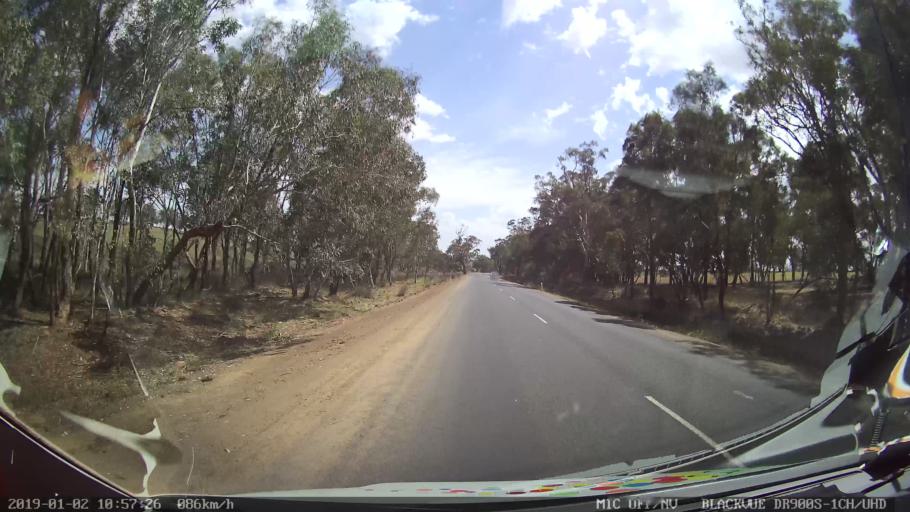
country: AU
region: New South Wales
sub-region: Cootamundra
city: Cootamundra
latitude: -34.6353
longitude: 148.2827
